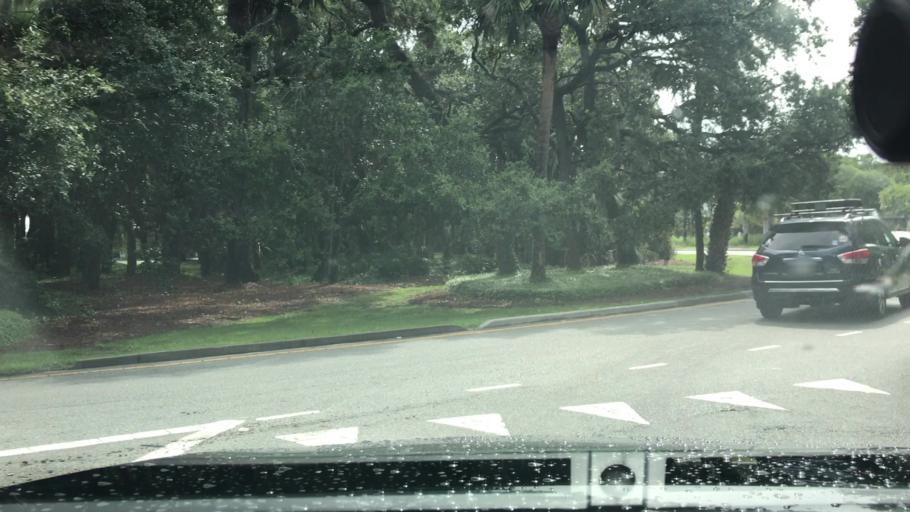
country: US
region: South Carolina
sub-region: Beaufort County
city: Hilton Head Island
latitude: 32.1421
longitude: -80.7522
